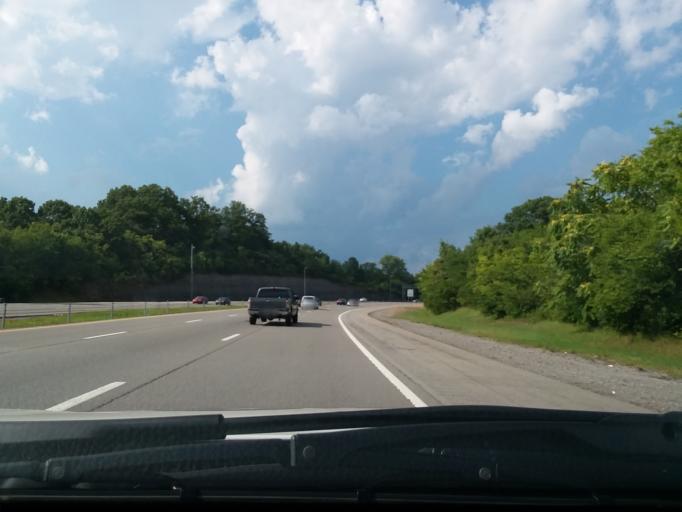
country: US
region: Tennessee
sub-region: Davidson County
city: Nashville
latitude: 36.2319
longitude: -86.7472
